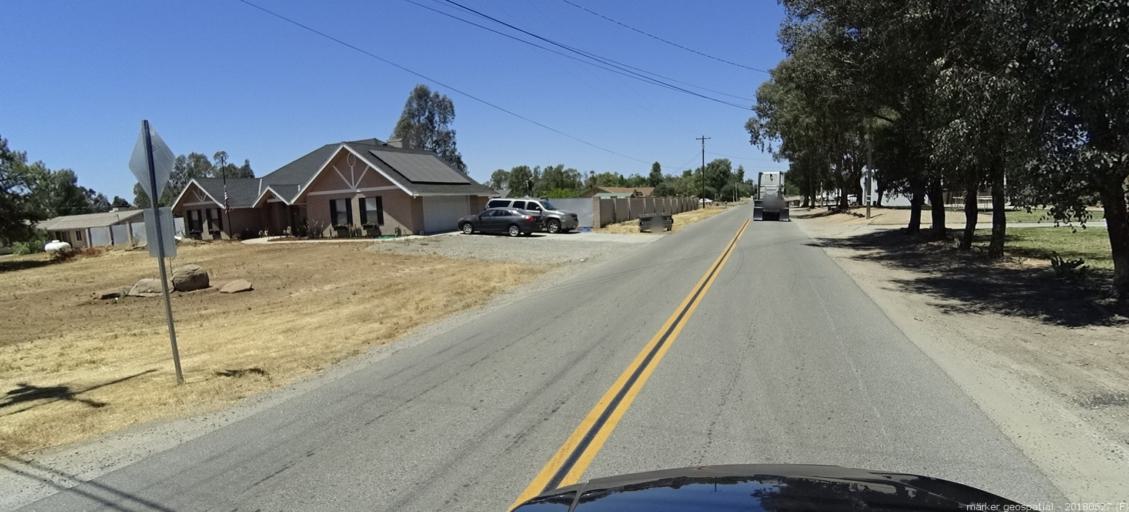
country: US
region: California
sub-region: Madera County
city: Bonadelle Ranchos-Madera Ranchos
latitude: 36.9249
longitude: -119.8625
